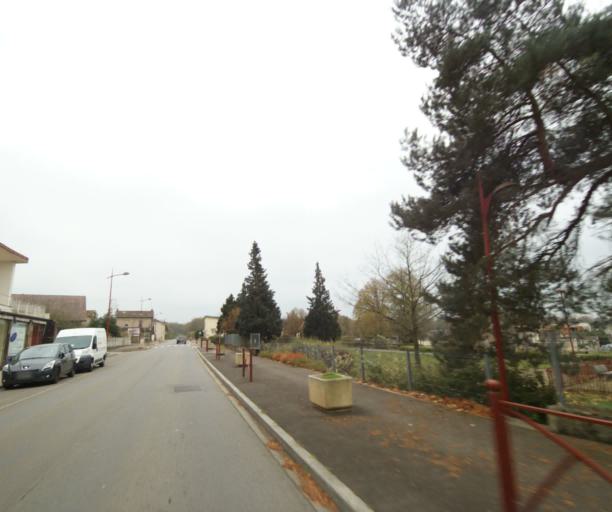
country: FR
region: Lorraine
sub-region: Departement de Meurthe-et-Moselle
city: Moutiers
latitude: 49.2362
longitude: 5.9738
